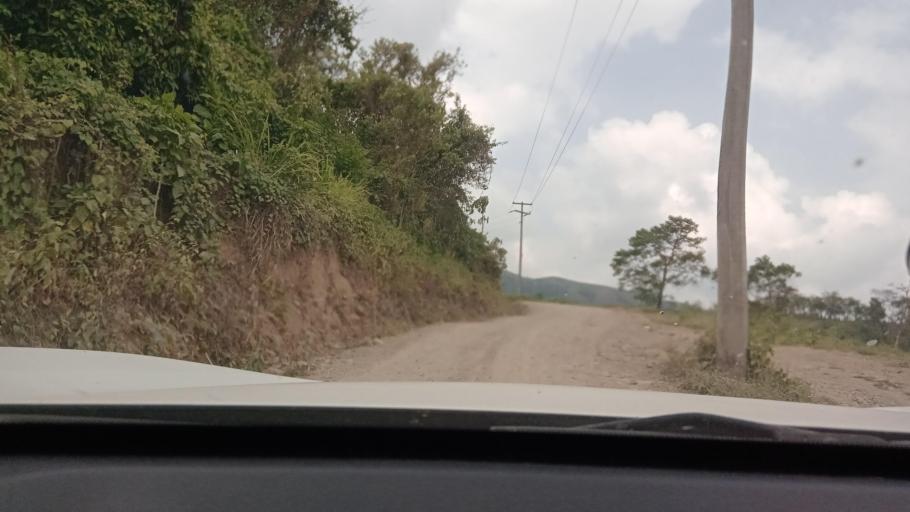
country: MX
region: Tabasco
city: Chontalpa
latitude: 17.4991
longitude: -93.6478
